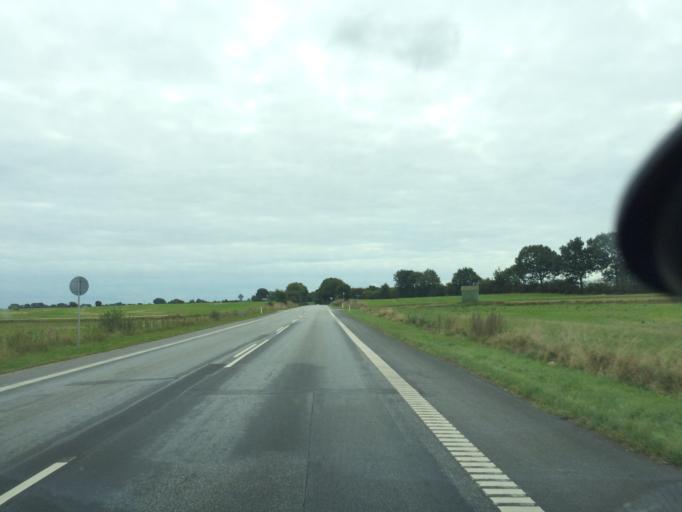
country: DK
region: South Denmark
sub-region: Sonderborg Kommune
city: Grasten
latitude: 54.9858
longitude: 9.6070
